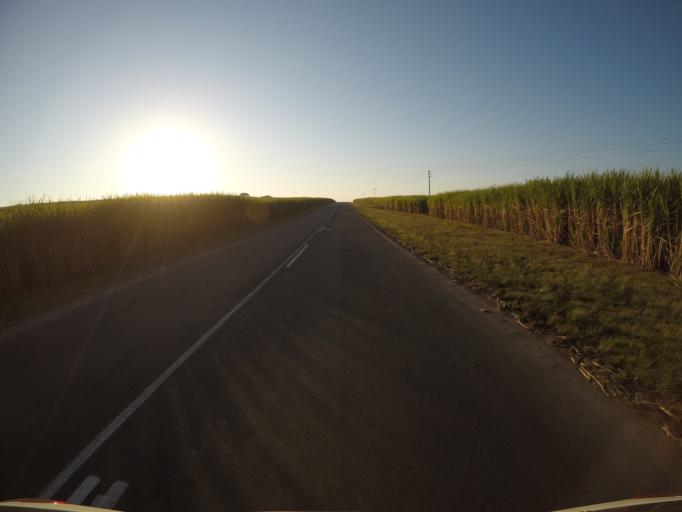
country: ZA
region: KwaZulu-Natal
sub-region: uThungulu District Municipality
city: eSikhawini
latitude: -28.9495
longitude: 31.7050
